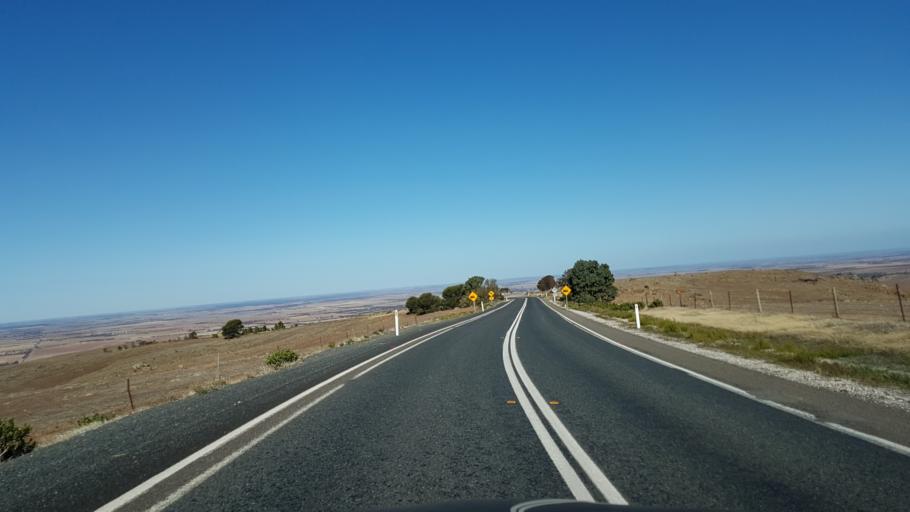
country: AU
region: South Australia
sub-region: Mid Murray
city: Mannum
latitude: -34.7571
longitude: 139.1796
